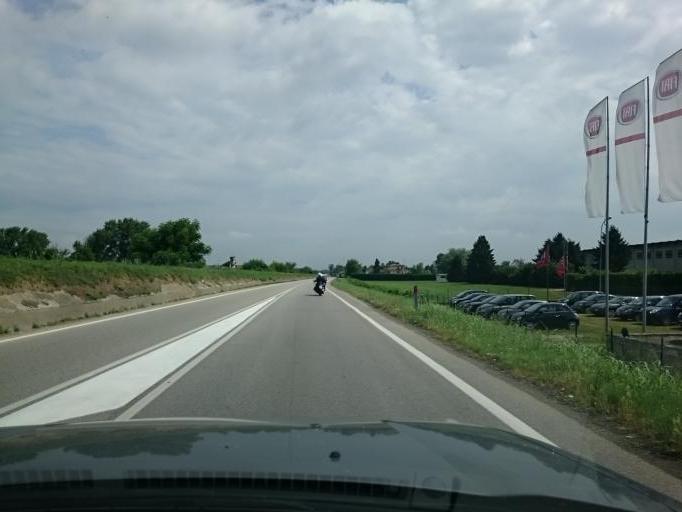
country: IT
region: Veneto
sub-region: Provincia di Padova
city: Terradura
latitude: 45.3455
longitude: 11.8289
